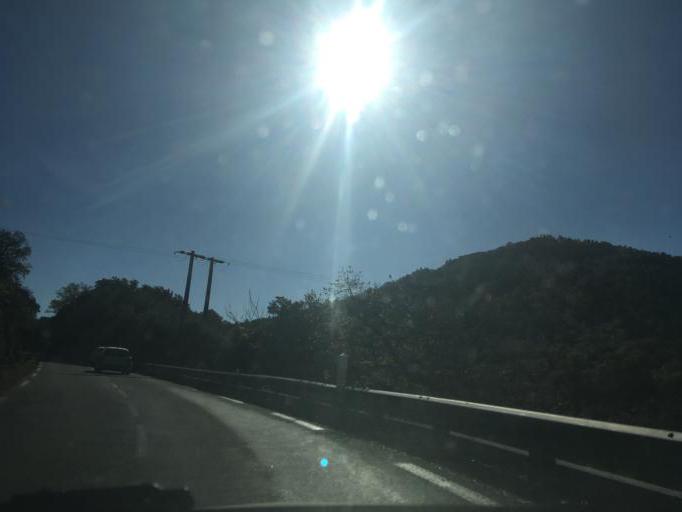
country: FR
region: Provence-Alpes-Cote d'Azur
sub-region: Departement du Var
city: La Garde-Freinet
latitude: 43.3281
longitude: 6.4622
